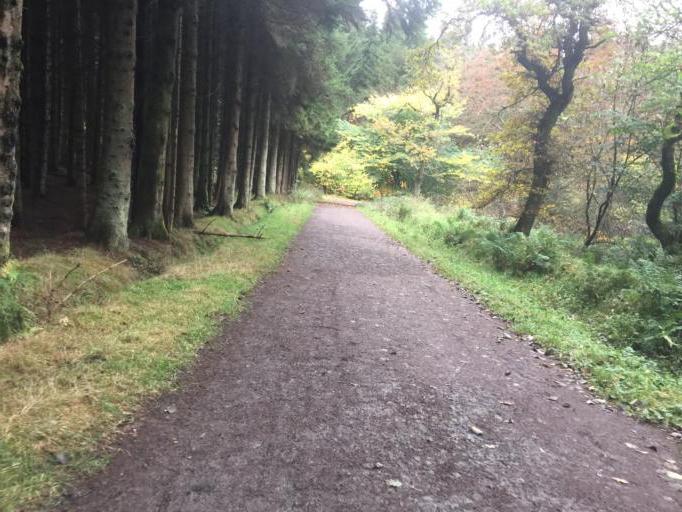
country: GB
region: Scotland
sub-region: West Lothian
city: Linlithgow
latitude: 55.9484
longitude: -3.5971
